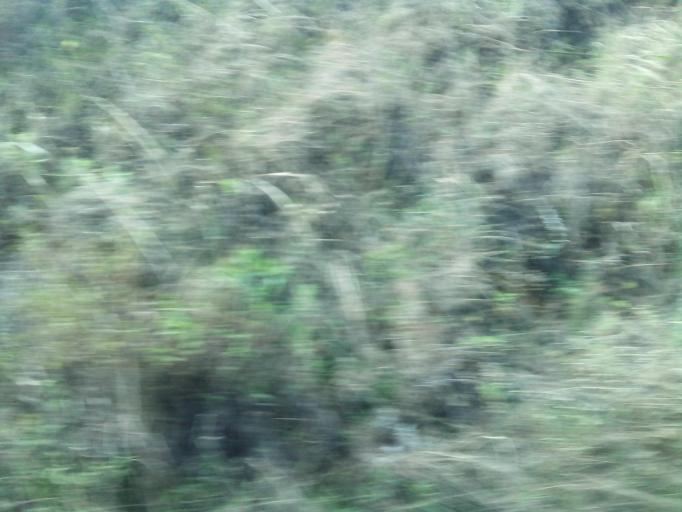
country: BR
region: Minas Gerais
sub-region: Belo Horizonte
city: Belo Horizonte
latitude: -19.8730
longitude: -43.8464
